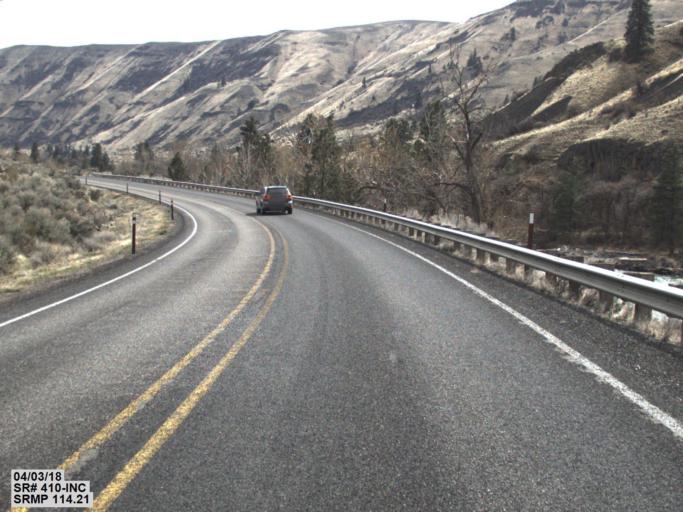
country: US
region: Washington
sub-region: Yakima County
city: Tieton
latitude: 46.7595
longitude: -120.8295
